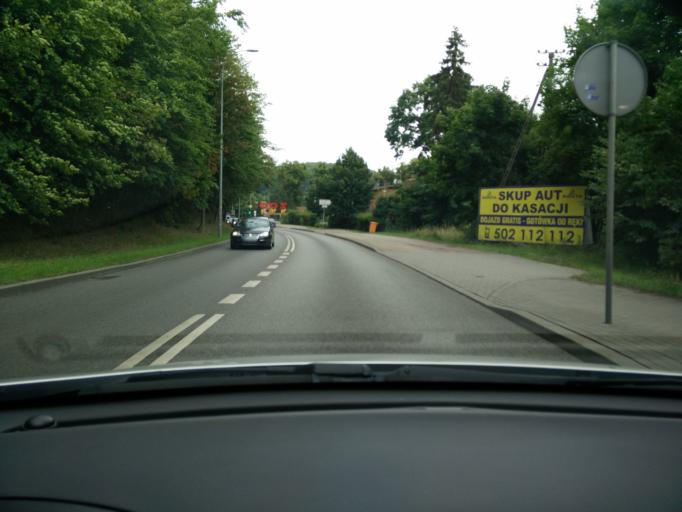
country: PL
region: Pomeranian Voivodeship
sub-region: Sopot
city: Sopot
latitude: 54.4126
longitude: 18.5473
